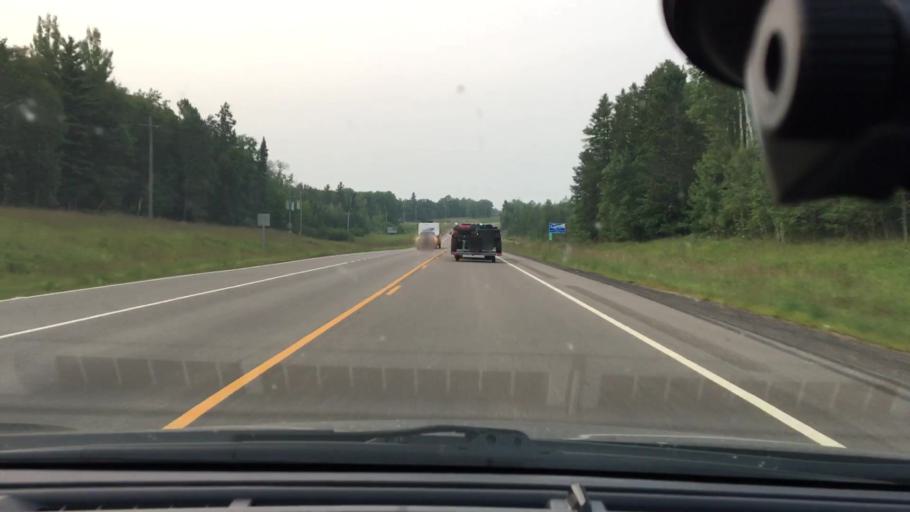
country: US
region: Minnesota
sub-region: Crow Wing County
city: Crosby
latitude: 46.5951
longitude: -93.9527
